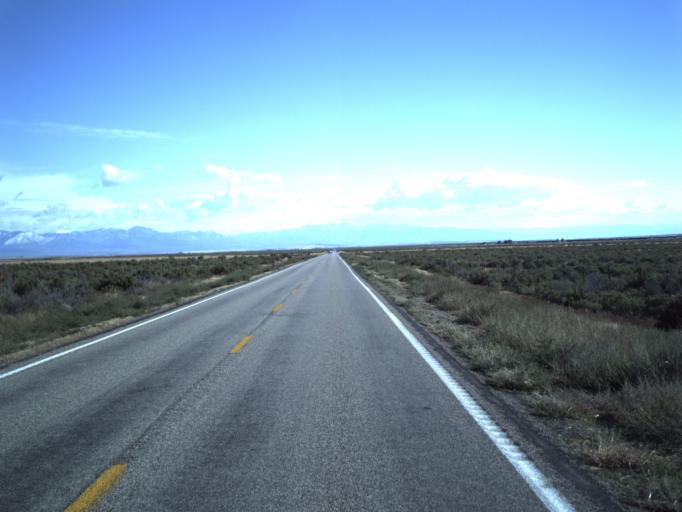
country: US
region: Utah
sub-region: Millard County
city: Delta
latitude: 39.3393
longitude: -112.4915
